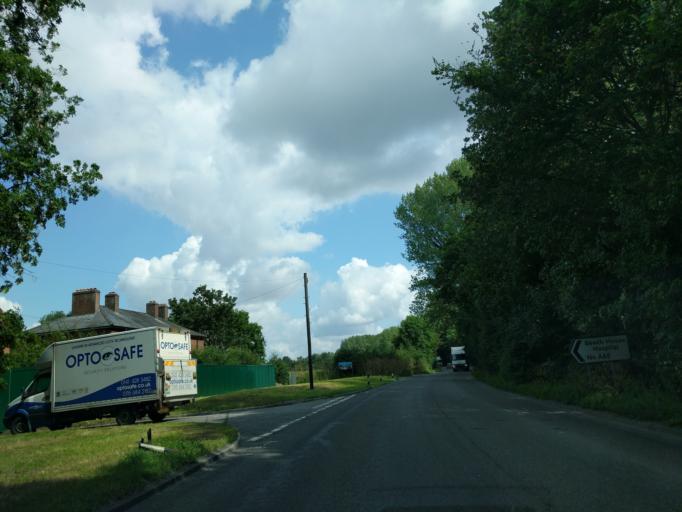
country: GB
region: England
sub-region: Suffolk
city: Exning
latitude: 52.2724
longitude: 0.3920
